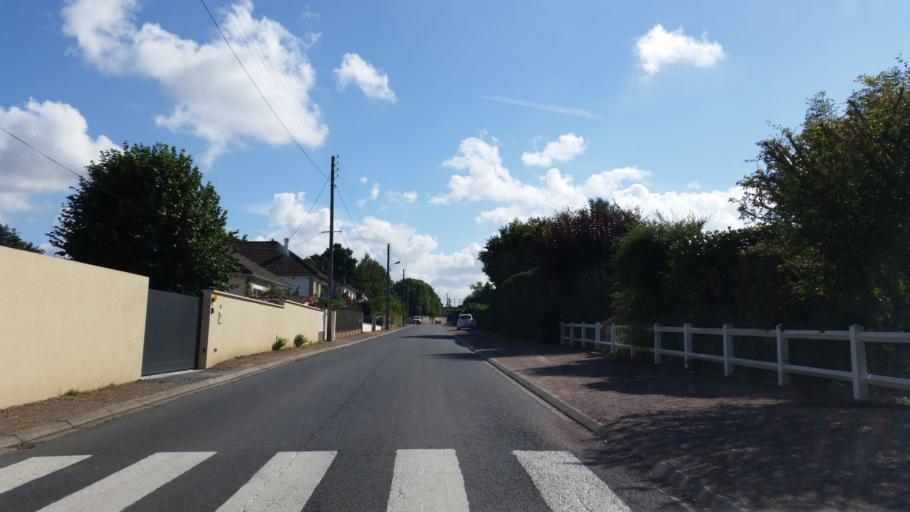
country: FR
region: Lower Normandy
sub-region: Departement du Calvados
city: Amfreville
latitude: 49.2531
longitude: -0.2304
